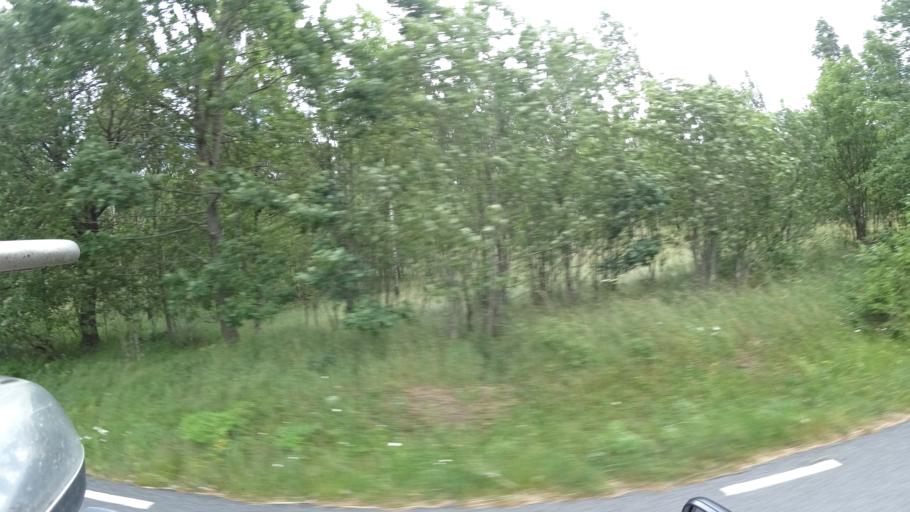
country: SE
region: Skane
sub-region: Kristianstads Kommun
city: Degeberga
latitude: 55.7208
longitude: 13.9931
